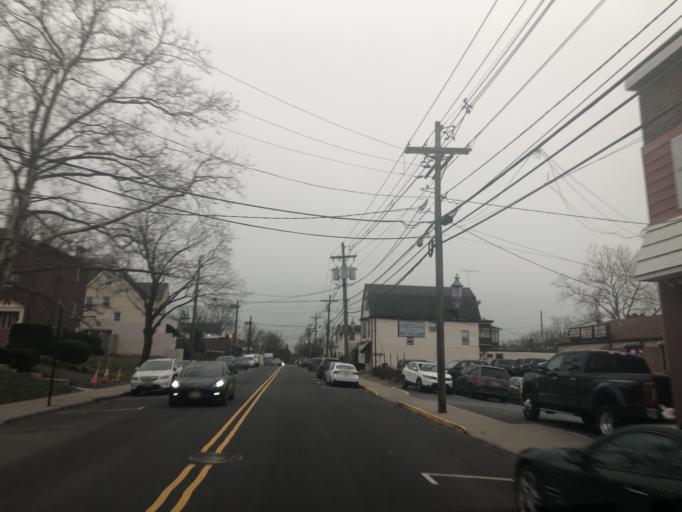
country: US
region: New Jersey
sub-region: Essex County
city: South Orange
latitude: 40.7401
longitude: -74.2638
